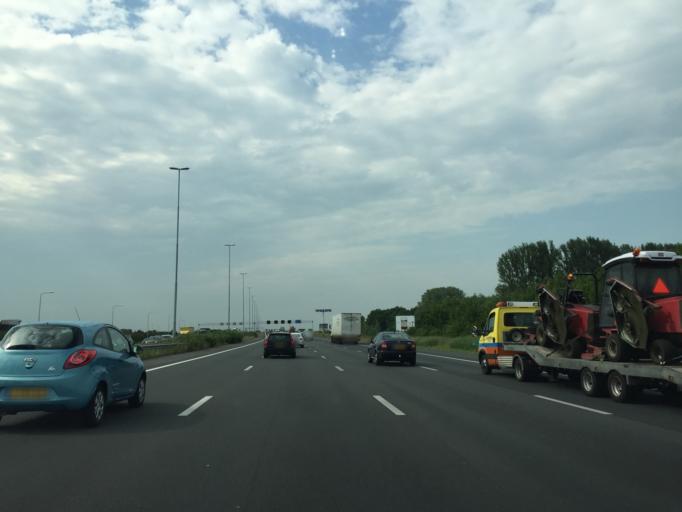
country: NL
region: Gelderland
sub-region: Gemeente Culemborg
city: Culemborg
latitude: 51.8942
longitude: 5.1955
